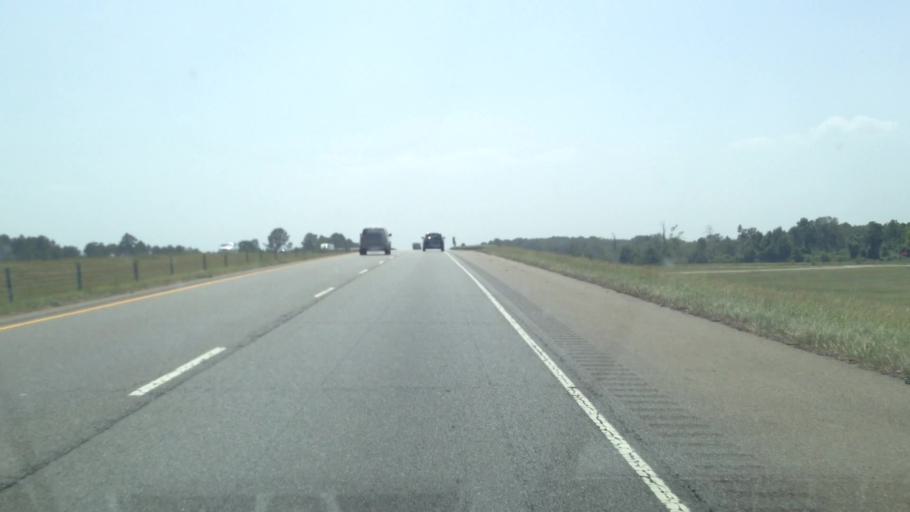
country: US
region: Louisiana
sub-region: Bossier Parish
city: Haughton
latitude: 32.5793
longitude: -93.4296
